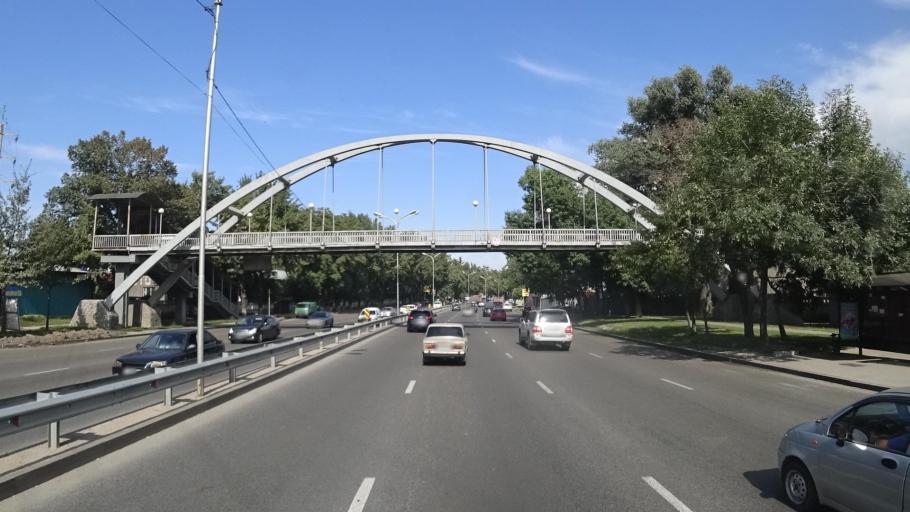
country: KZ
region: Almaty Qalasy
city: Almaty
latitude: 43.2891
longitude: 76.9259
